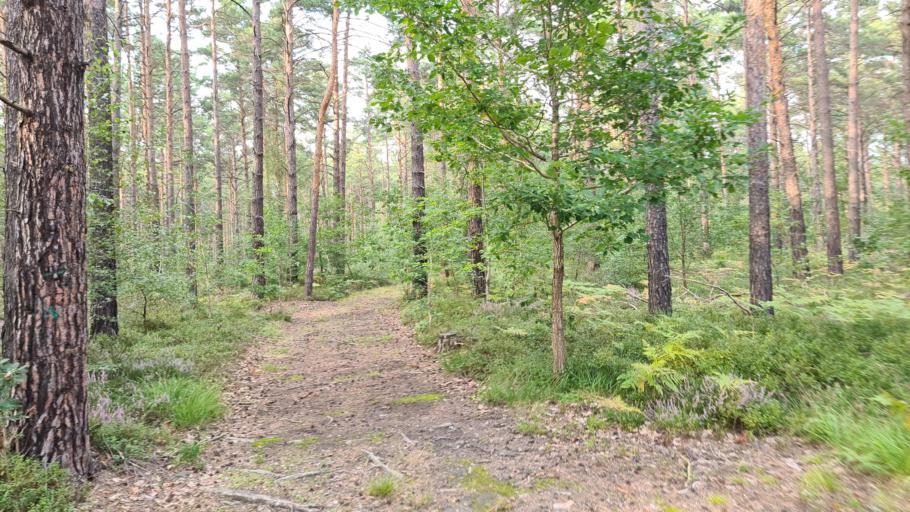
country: DE
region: Brandenburg
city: Trobitz
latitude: 51.6151
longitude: 13.4419
